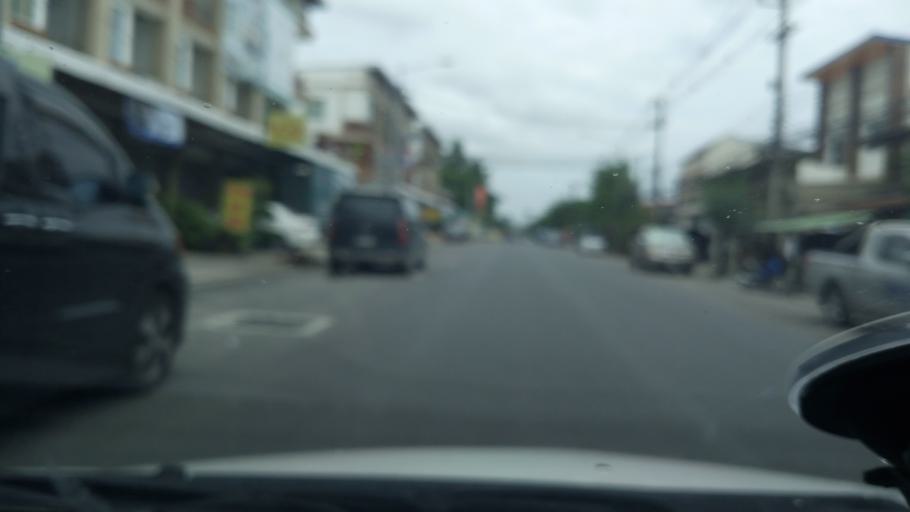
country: TH
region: Chon Buri
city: Chon Buri
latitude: 13.3480
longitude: 101.0045
